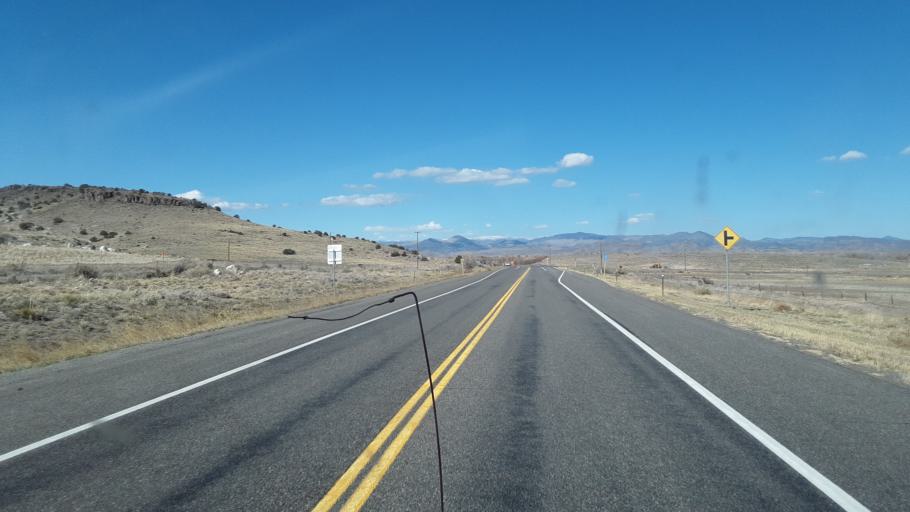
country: US
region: Colorado
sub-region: Rio Grande County
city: Del Norte
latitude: 37.6468
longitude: -106.2712
